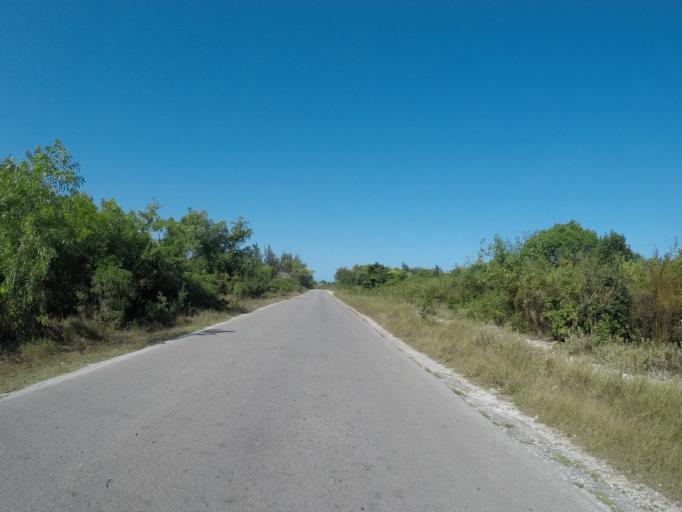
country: TZ
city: Kiwengwa
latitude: -6.1427
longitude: 39.5086
